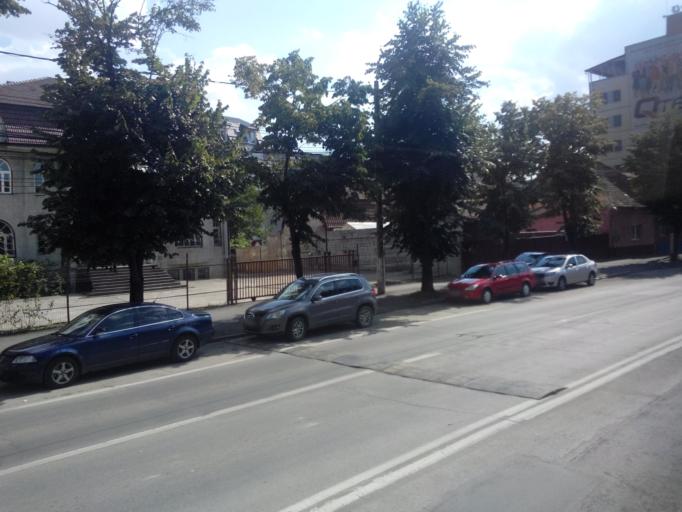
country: RO
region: Timis
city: Timisoara
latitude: 45.7637
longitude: 21.2555
